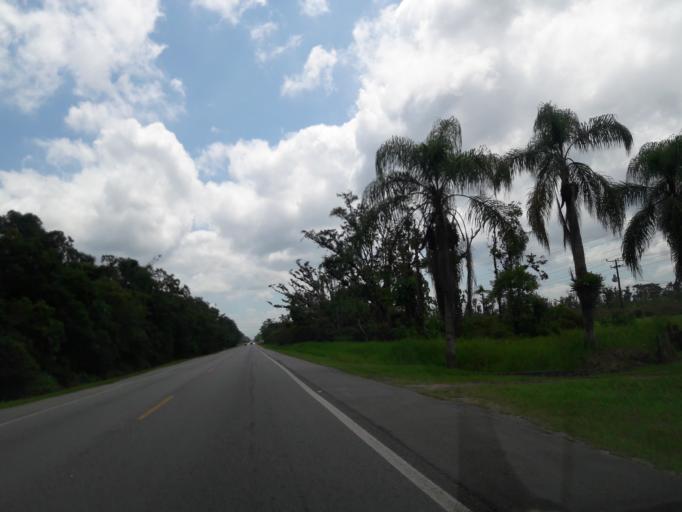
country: BR
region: Parana
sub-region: Pontal Do Parana
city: Pontal do Parana
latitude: -25.6474
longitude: -48.5292
